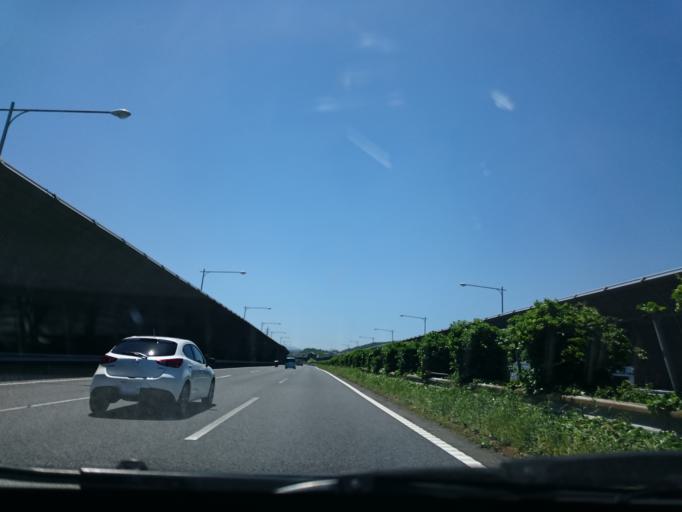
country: JP
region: Kanagawa
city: Isehara
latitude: 35.3840
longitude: 139.2739
